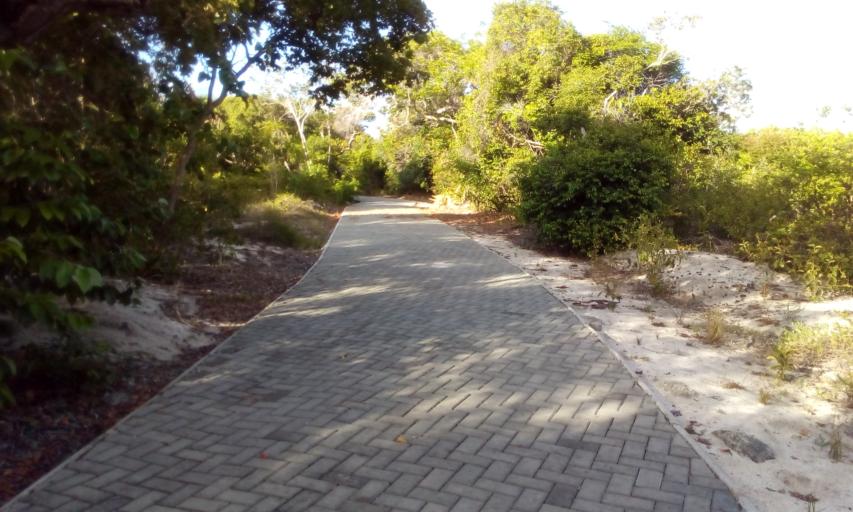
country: BR
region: Bahia
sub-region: Mata De Sao Joao
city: Mata de Sao Joao
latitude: -12.5717
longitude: -38.0072
